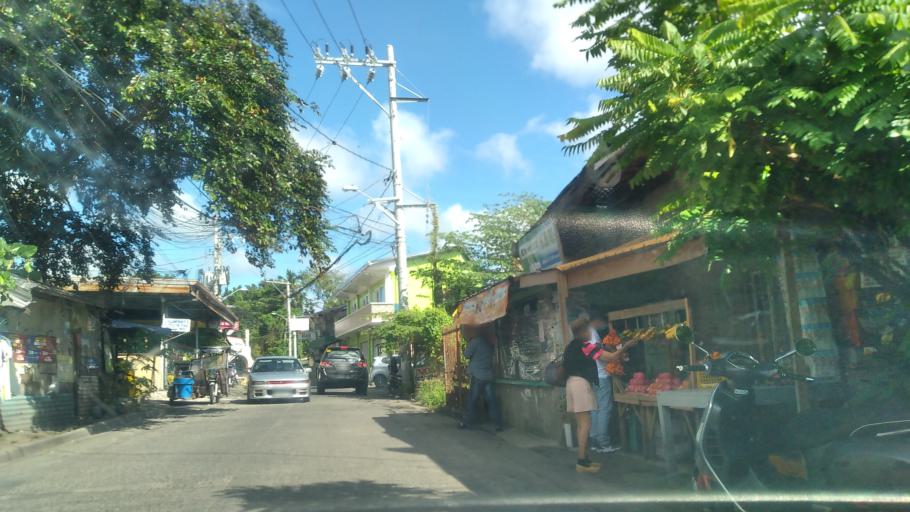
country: PH
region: Calabarzon
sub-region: Province of Quezon
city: Lucena
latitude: 13.9401
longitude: 121.6119
